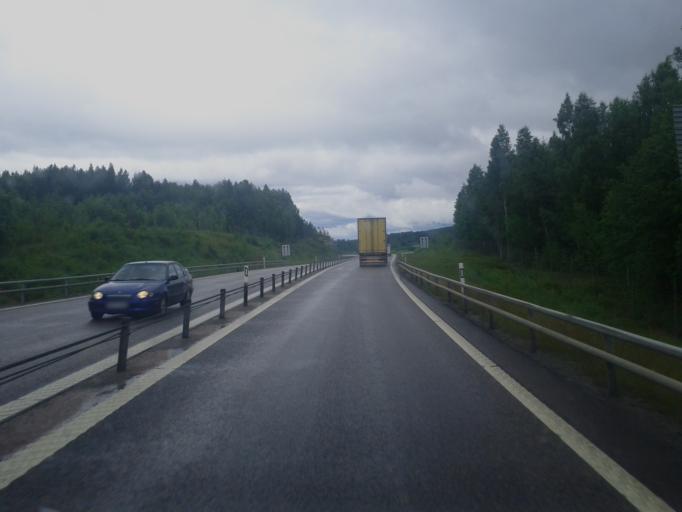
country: SE
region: Vaesternorrland
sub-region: Haernoesands Kommun
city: Haernoesand
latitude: 62.7414
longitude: 17.9060
